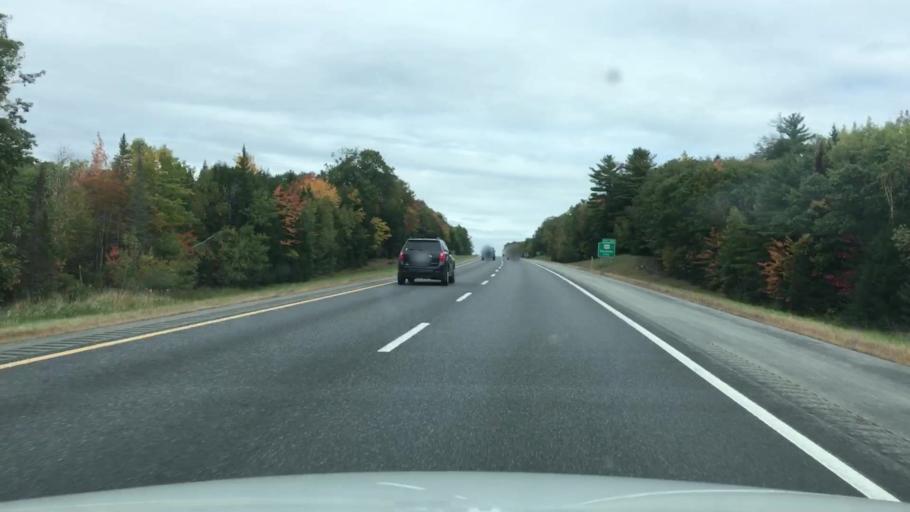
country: US
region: Maine
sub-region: Sagadahoc County
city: Richmond
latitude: 44.1612
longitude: -69.8349
